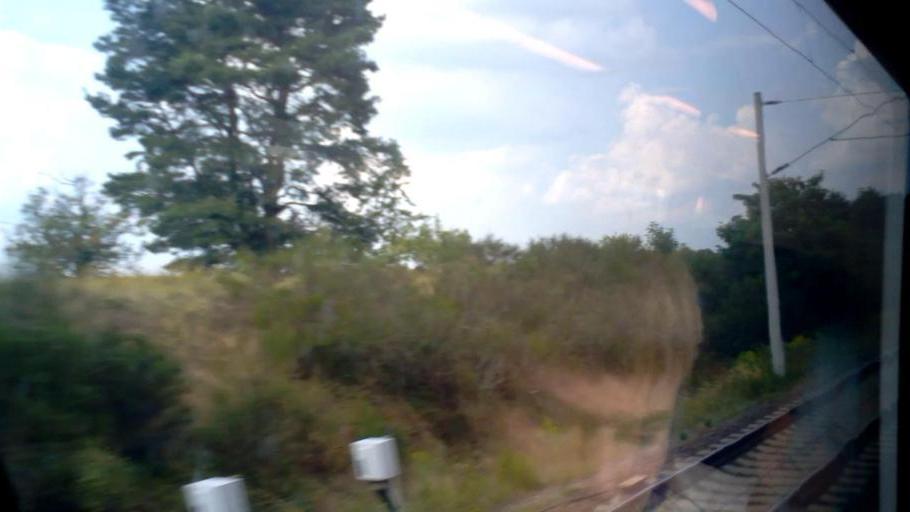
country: DE
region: Brandenburg
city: Grossbeeren
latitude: 52.3573
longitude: 13.2874
